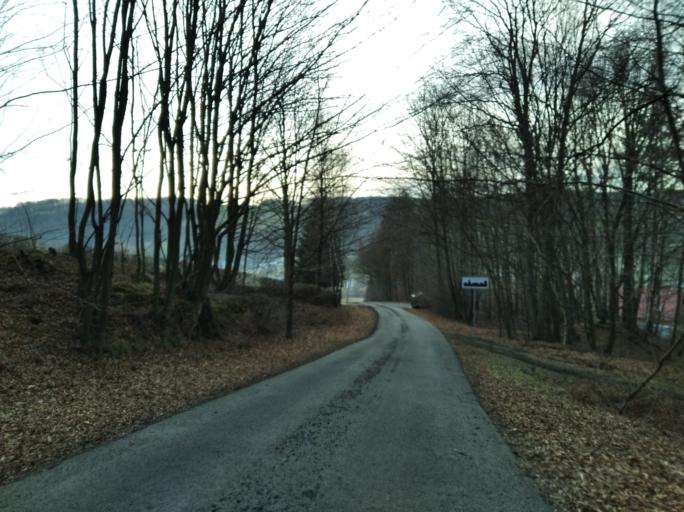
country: PL
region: Subcarpathian Voivodeship
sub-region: Powiat strzyzowski
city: Czudec
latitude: 49.9267
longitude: 21.7998
